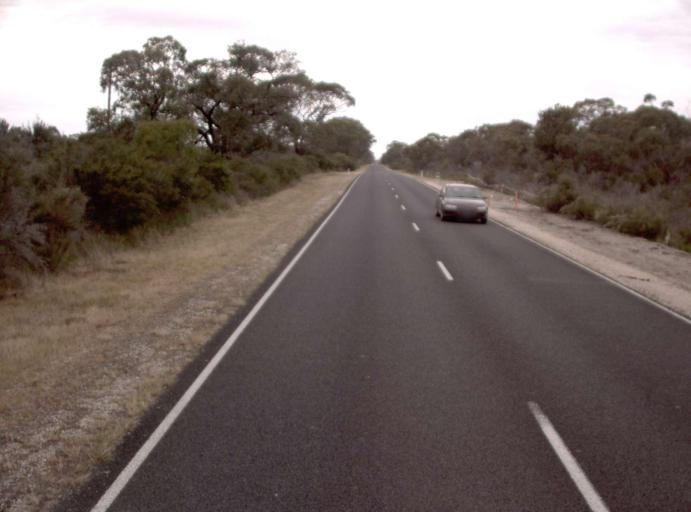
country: AU
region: Victoria
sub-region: Wellington
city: Sale
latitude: -38.1372
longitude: 147.4123
